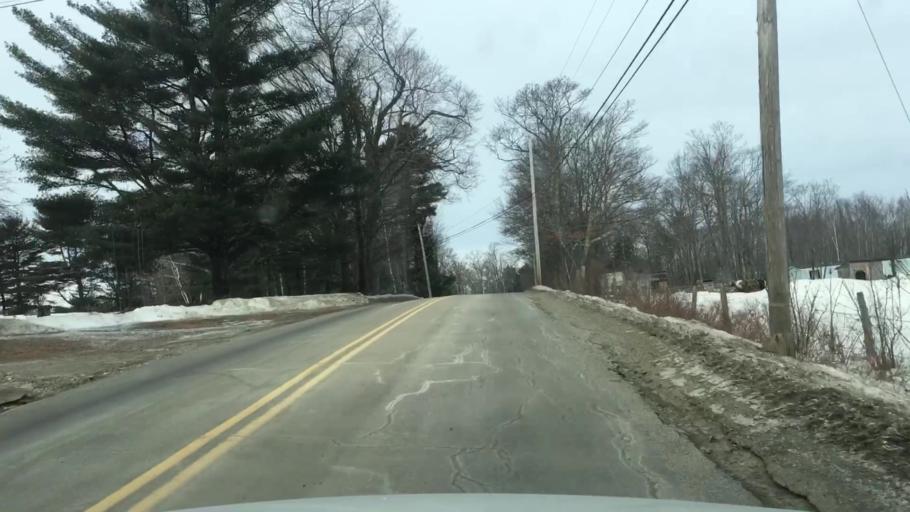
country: US
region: Maine
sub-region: Kennebec County
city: Chelsea
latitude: 44.2563
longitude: -69.6422
